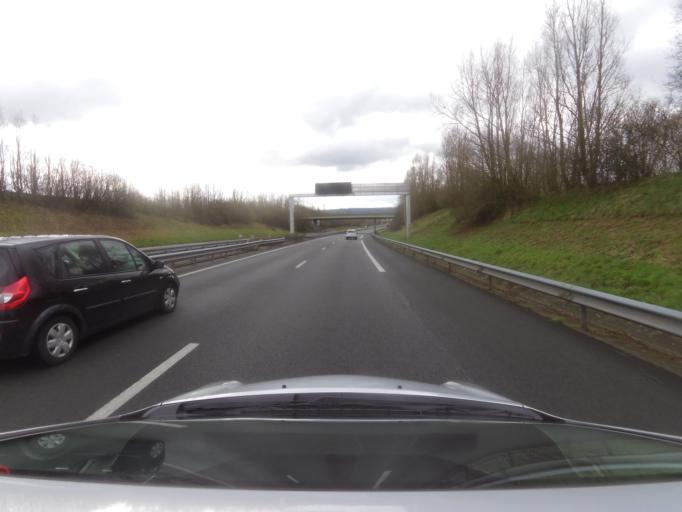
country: FR
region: Nord-Pas-de-Calais
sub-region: Departement du Pas-de-Calais
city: Isques
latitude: 50.6527
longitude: 1.6621
